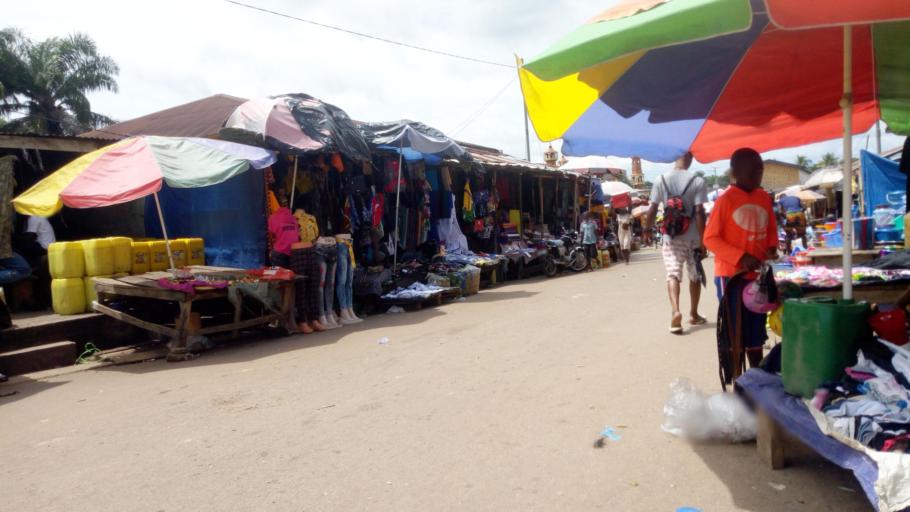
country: SL
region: Northern Province
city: Magburaka
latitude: 8.7231
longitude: -11.9502
